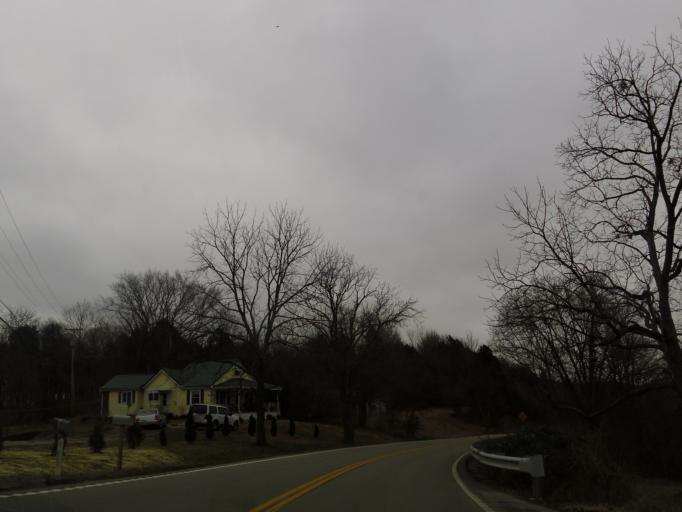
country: US
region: Kentucky
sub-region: Franklin County
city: Frankfort
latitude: 38.2177
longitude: -84.8969
